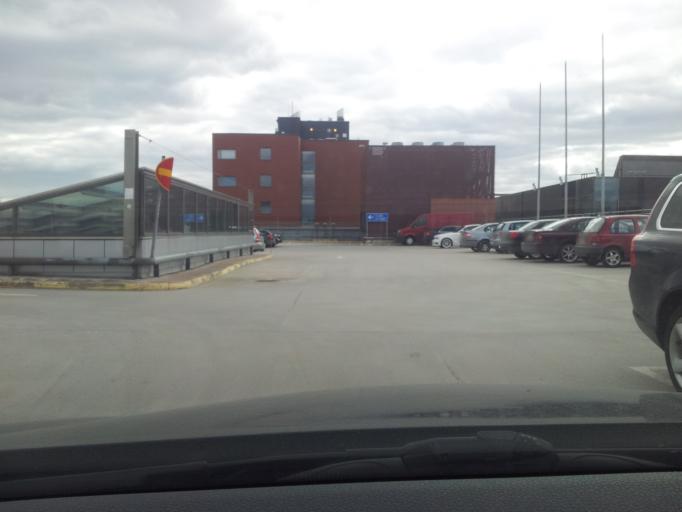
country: FI
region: Uusimaa
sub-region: Helsinki
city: Kilo
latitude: 60.2181
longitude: 24.8111
